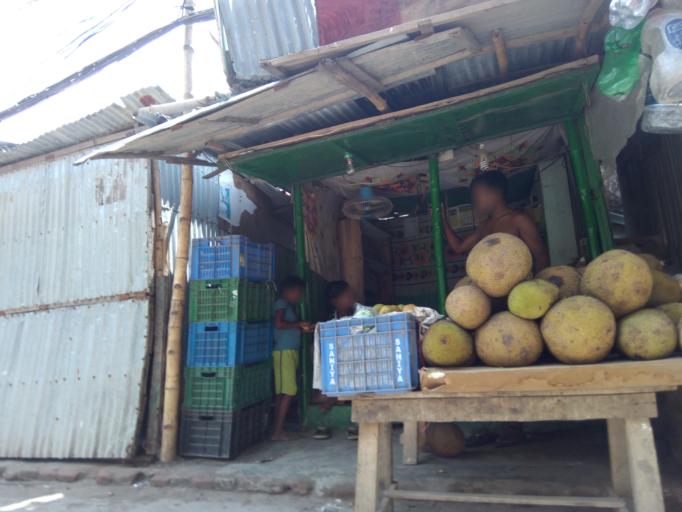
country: BD
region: Dhaka
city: Azimpur
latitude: 23.7292
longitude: 90.3604
